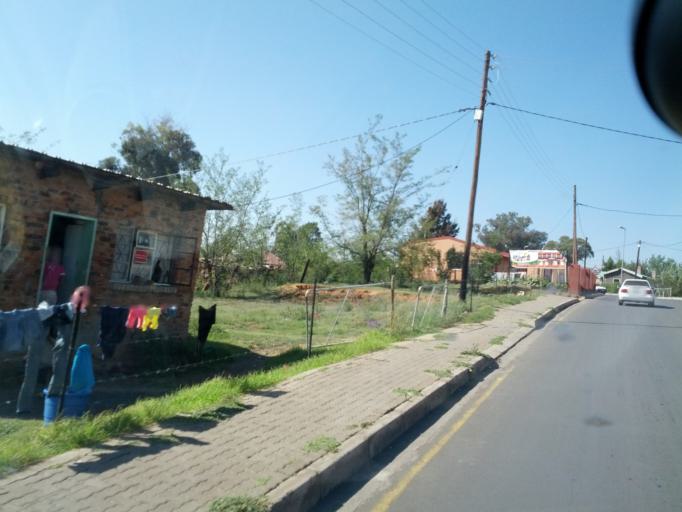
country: LS
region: Maseru
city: Maseru
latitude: -29.3036
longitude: 27.4939
